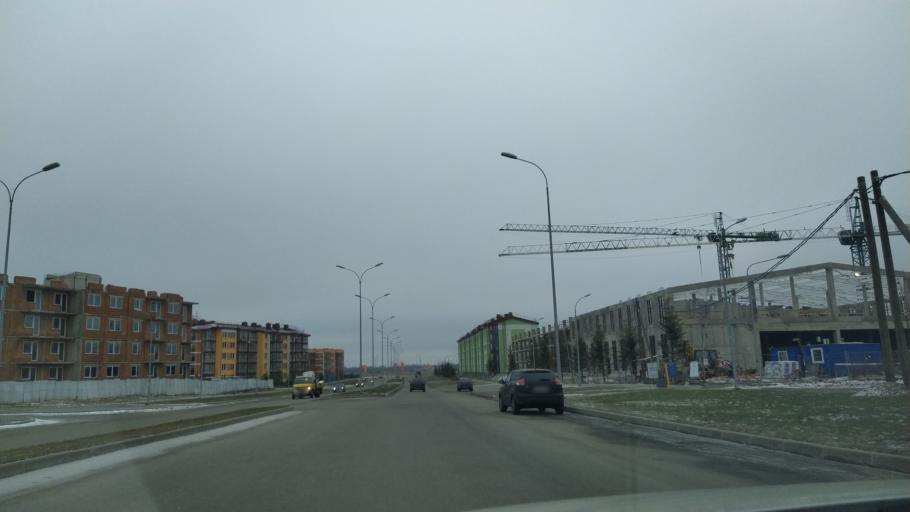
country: RU
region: St.-Petersburg
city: Aleksandrovskaya
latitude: 59.7582
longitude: 30.3686
